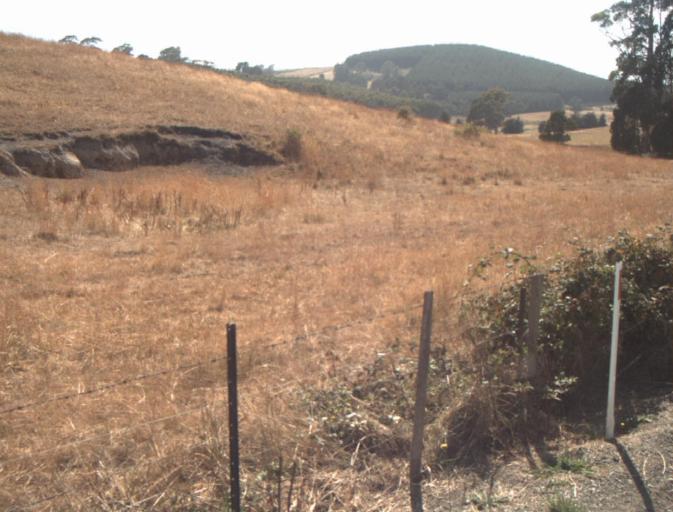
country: AU
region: Tasmania
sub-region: Launceston
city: Mayfield
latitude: -41.1759
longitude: 147.2156
